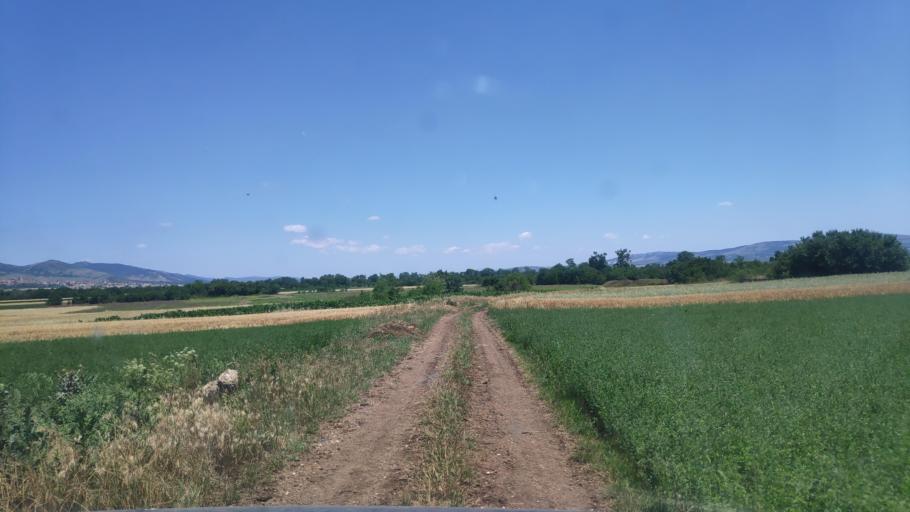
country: MK
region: Kumanovo
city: Bedinje
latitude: 42.1666
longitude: 21.6844
